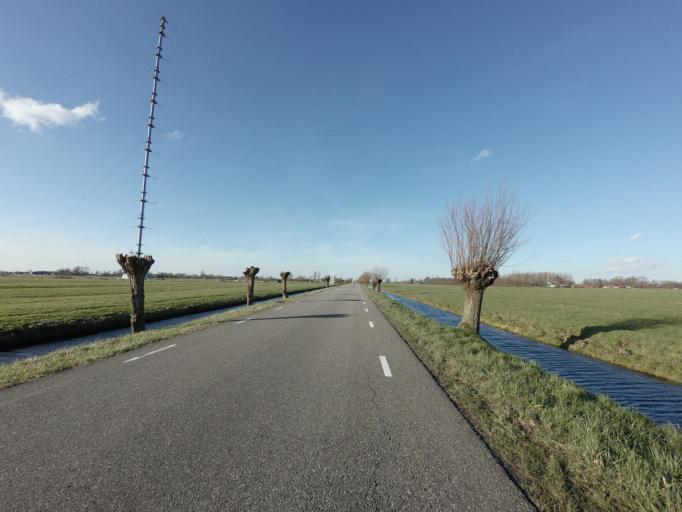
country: NL
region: Utrecht
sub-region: Gemeente Lopik
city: Lopik
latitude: 51.9691
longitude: 4.9295
